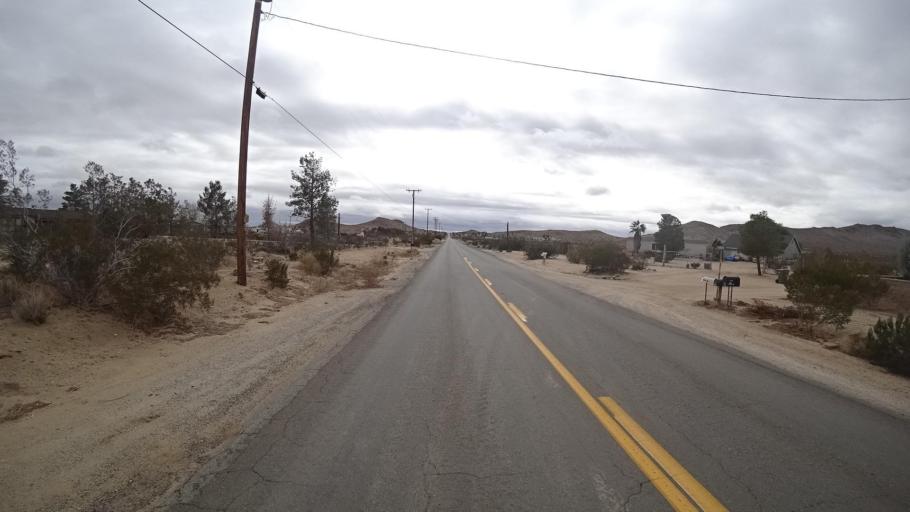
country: US
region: California
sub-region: Kern County
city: Rosamond
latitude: 34.9346
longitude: -118.2124
